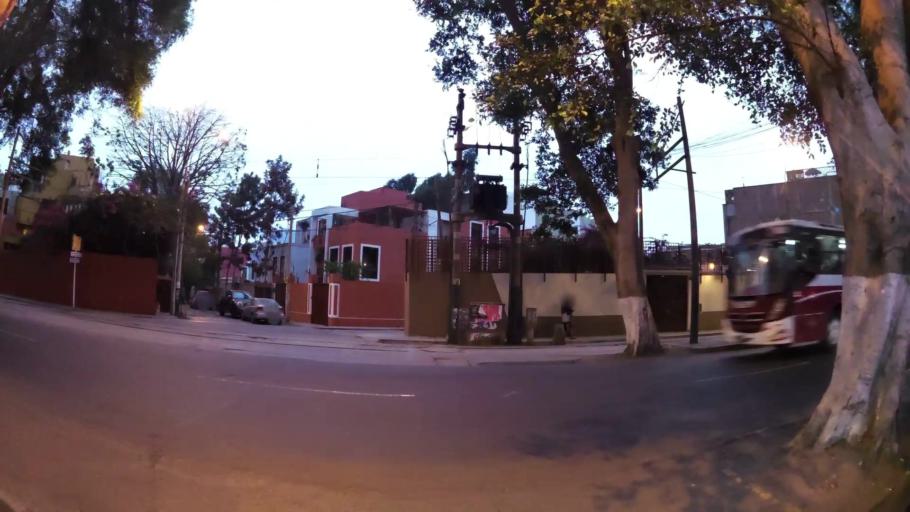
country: PE
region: Lima
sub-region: Lima
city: Surco
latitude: -12.1519
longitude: -77.0224
